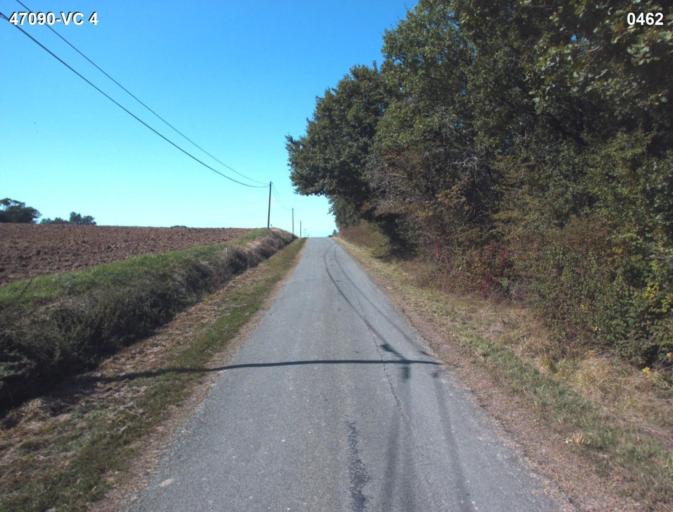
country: FR
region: Aquitaine
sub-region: Departement du Lot-et-Garonne
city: Vianne
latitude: 44.1774
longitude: 0.3486
